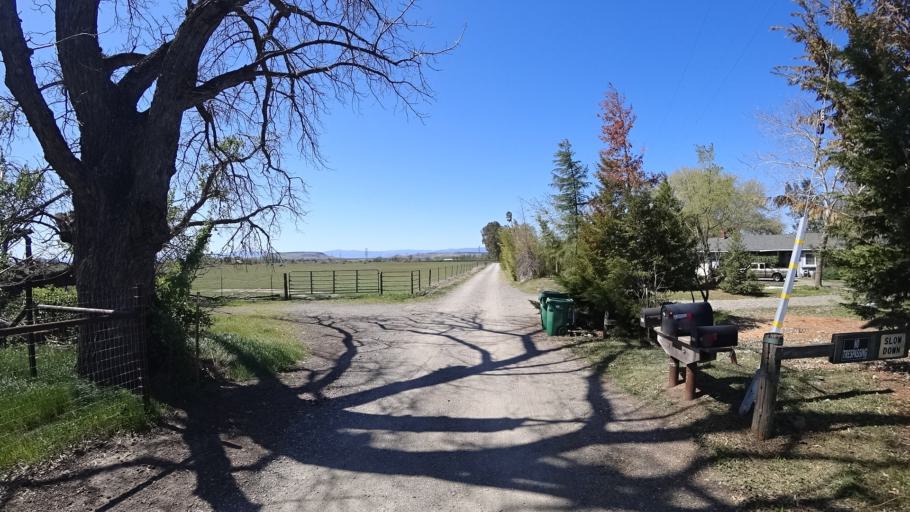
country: US
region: California
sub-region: Glenn County
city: Orland
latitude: 39.7843
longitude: -122.2569
